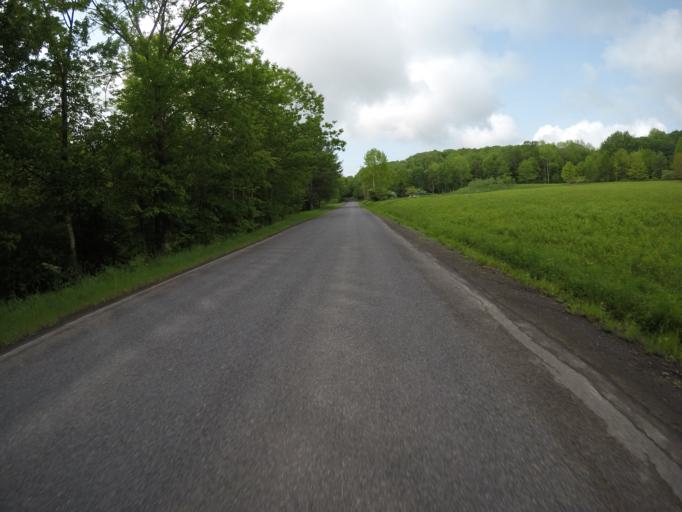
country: US
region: New York
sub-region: Delaware County
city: Stamford
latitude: 42.1500
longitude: -74.6716
